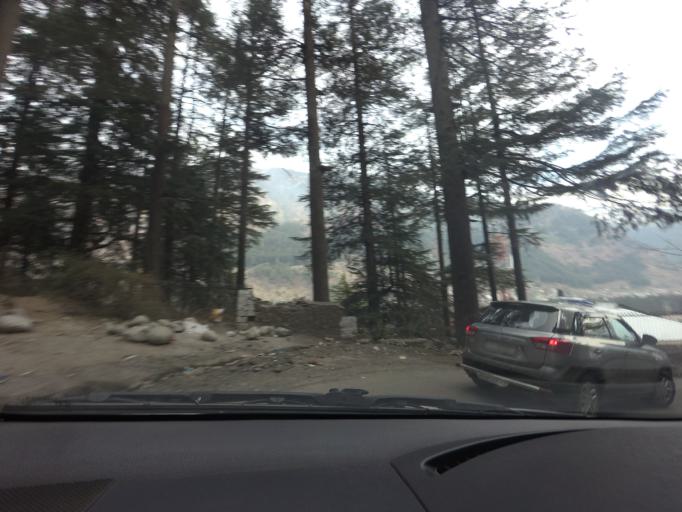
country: IN
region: Himachal Pradesh
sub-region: Kulu
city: Manali
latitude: 32.2474
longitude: 77.1836
